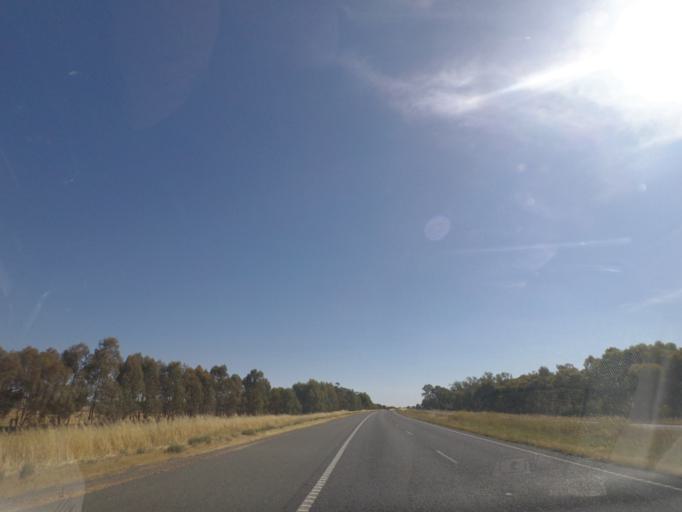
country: AU
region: Victoria
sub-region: Greater Shepparton
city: Shepparton
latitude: -36.6608
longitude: 145.2796
